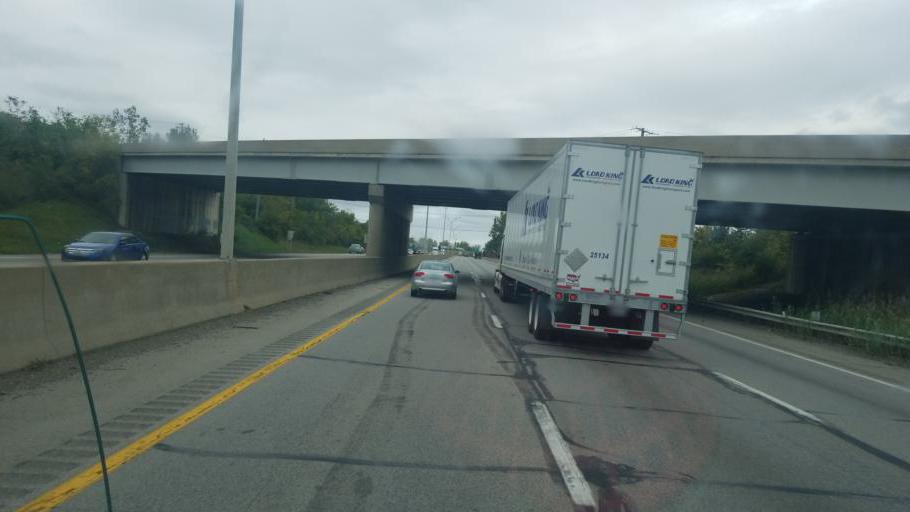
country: US
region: Ohio
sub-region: Lucas County
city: Oregon
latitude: 41.7124
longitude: -83.5019
